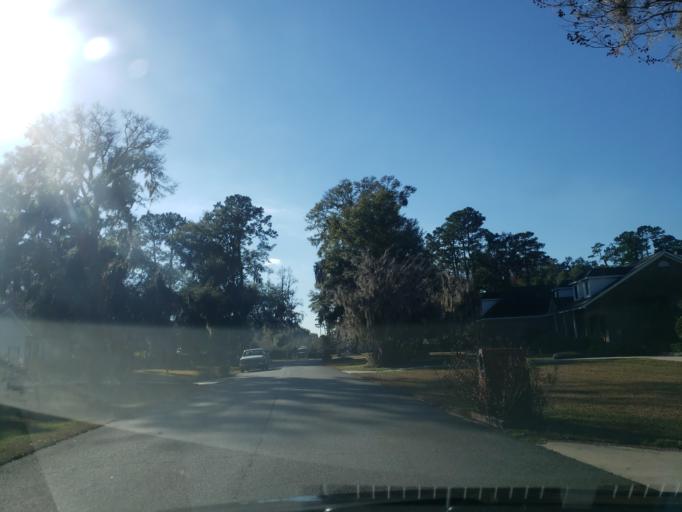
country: US
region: Georgia
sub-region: Chatham County
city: Whitemarsh Island
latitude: 32.0599
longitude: -81.0168
